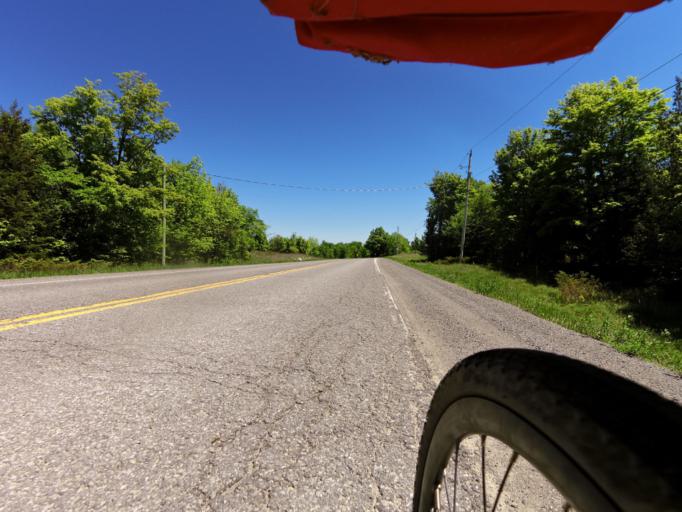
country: CA
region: Ontario
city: Carleton Place
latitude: 45.1838
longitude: -76.3713
